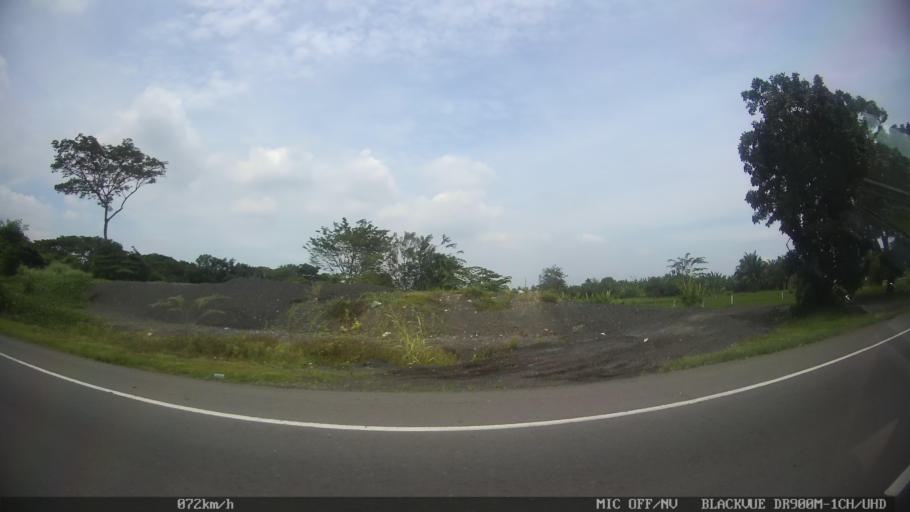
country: ID
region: North Sumatra
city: Labuhan Deli
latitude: 3.6978
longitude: 98.6818
